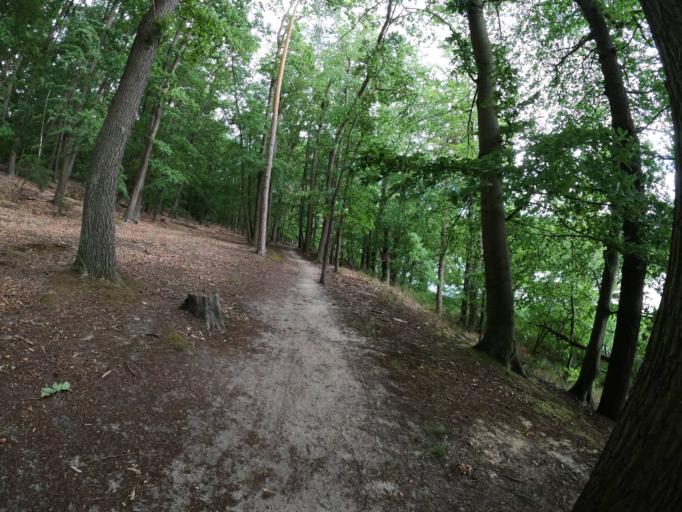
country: DE
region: Brandenburg
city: Angermunde
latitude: 53.0236
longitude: 13.9118
